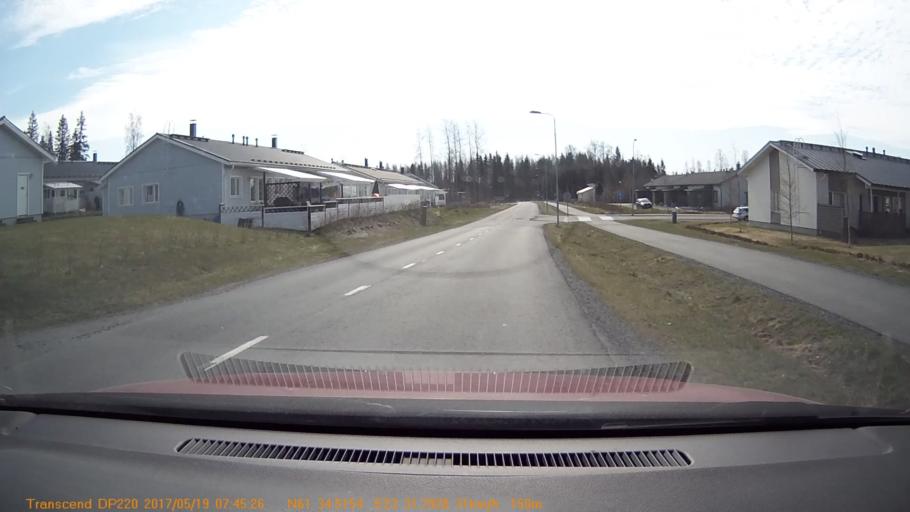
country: FI
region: Pirkanmaa
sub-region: Tampere
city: Yloejaervi
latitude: 61.5753
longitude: 23.5305
